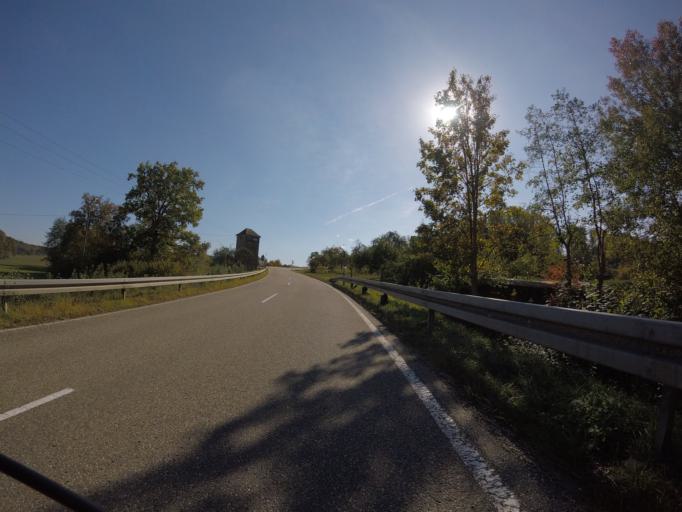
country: DE
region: Baden-Wuerttemberg
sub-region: Karlsruhe Region
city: Olbronn-Durrn
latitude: 48.9947
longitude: 8.7447
